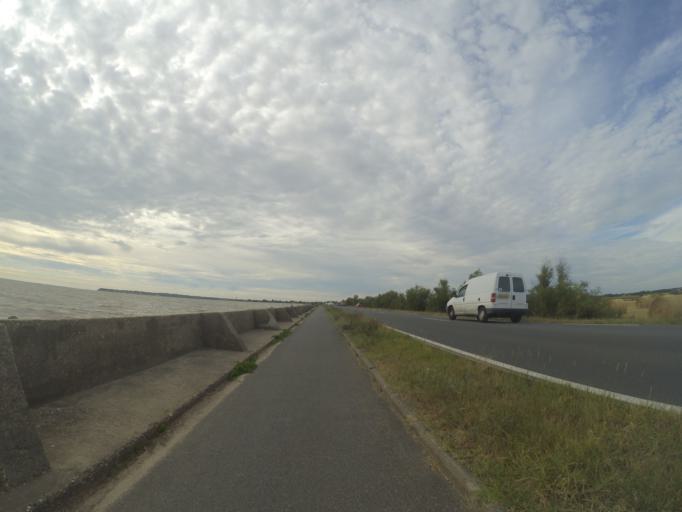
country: FR
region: Poitou-Charentes
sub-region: Departement de la Charente-Maritime
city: Meschers-sur-Gironde
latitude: 45.5424
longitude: -0.9088
